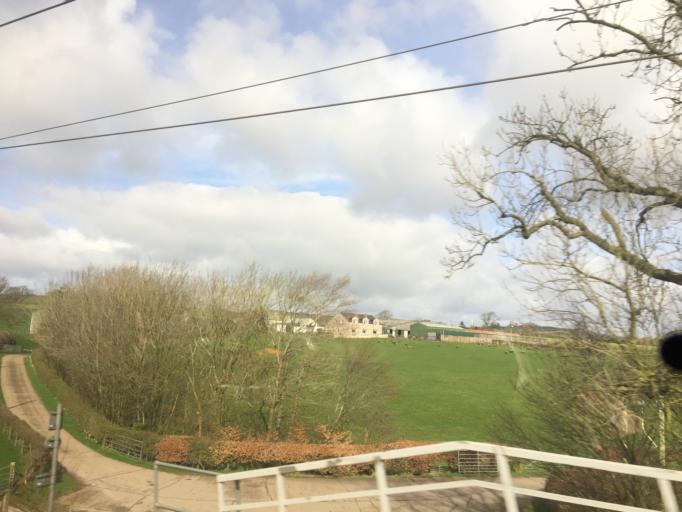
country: GB
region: Scotland
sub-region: Dumfries and Galloway
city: Annan
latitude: 55.0644
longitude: -3.2298
